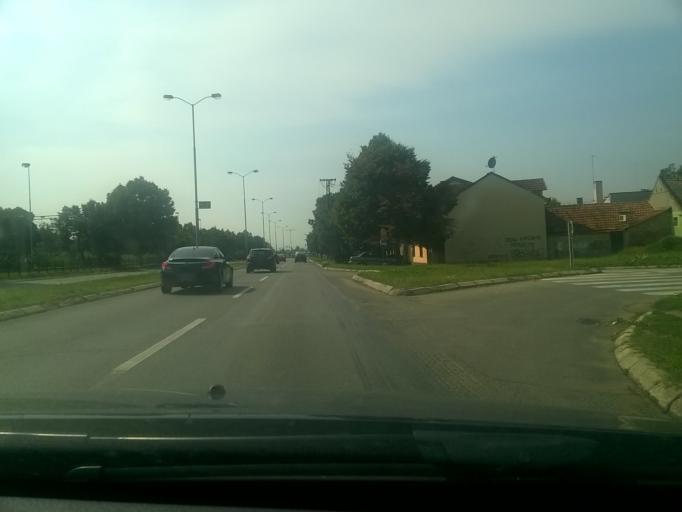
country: RS
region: Autonomna Pokrajina Vojvodina
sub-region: Juznobanatski Okrug
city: Pancevo
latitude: 44.8602
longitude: 20.6558
